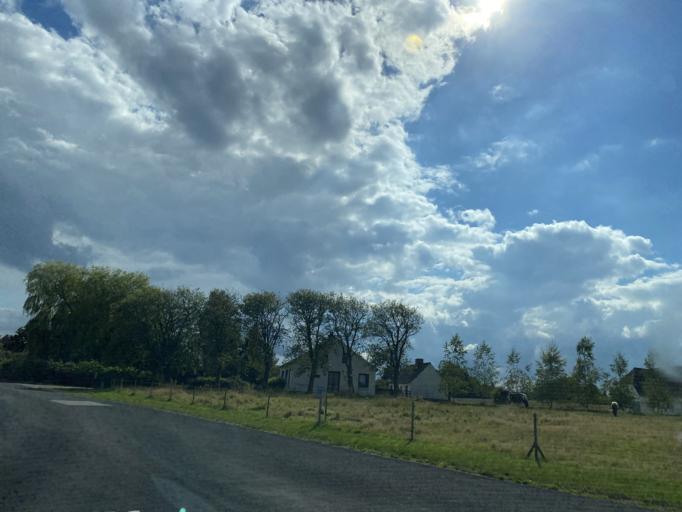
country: DK
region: South Denmark
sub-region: Haderslev Kommune
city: Starup
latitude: 55.2068
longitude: 9.5163
